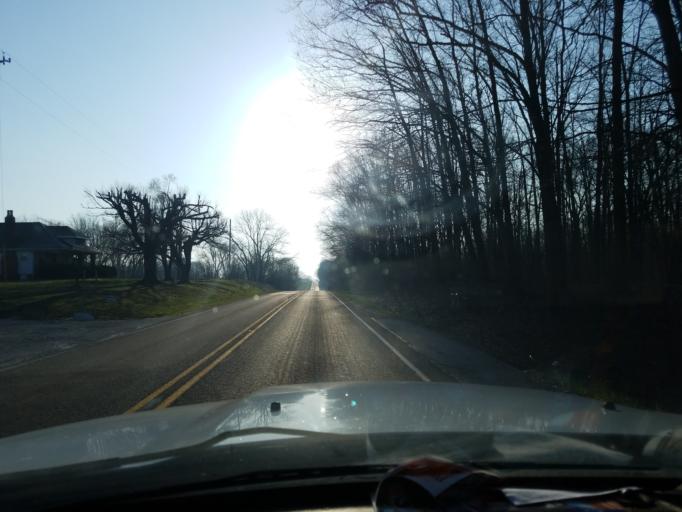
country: US
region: Indiana
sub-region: Clay County
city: Middlebury
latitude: 39.3882
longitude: -87.1713
